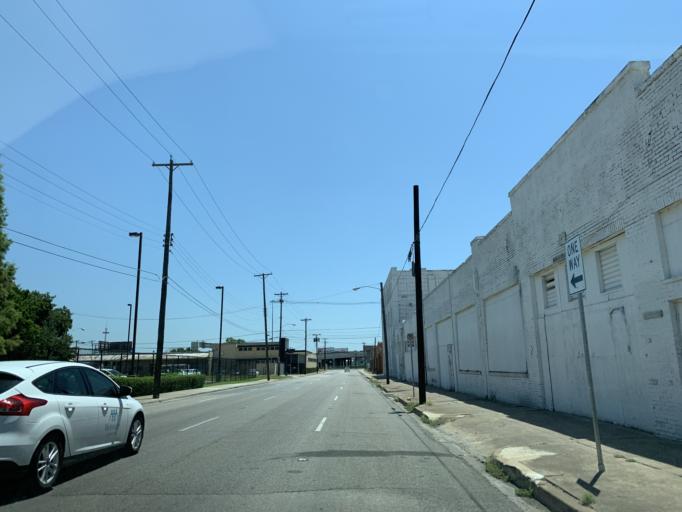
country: US
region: Texas
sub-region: Dallas County
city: Dallas
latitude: 32.7832
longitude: -96.7736
